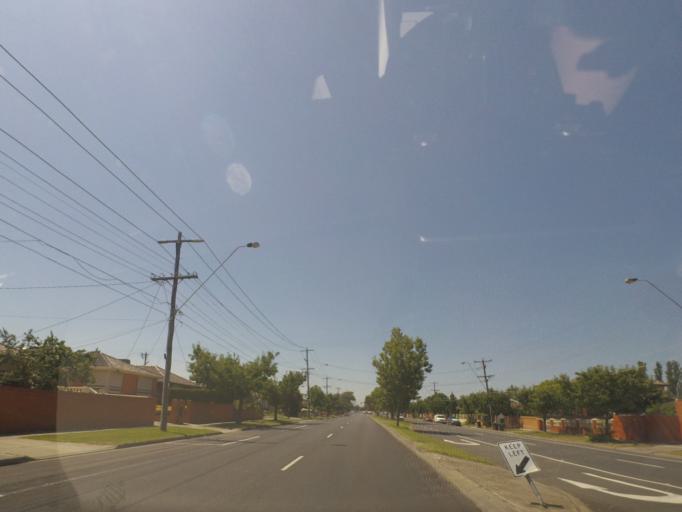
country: AU
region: Victoria
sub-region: Whittlesea
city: Thomastown
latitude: -37.6812
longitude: 144.9989
